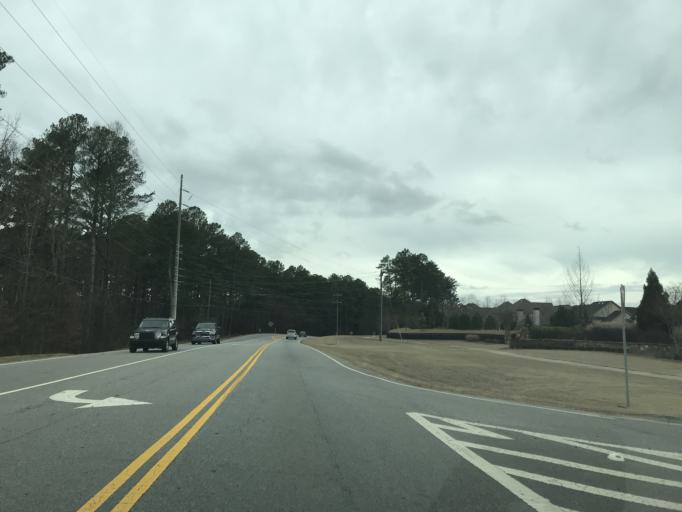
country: US
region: Georgia
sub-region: Forsyth County
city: Cumming
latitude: 34.1548
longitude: -84.2044
